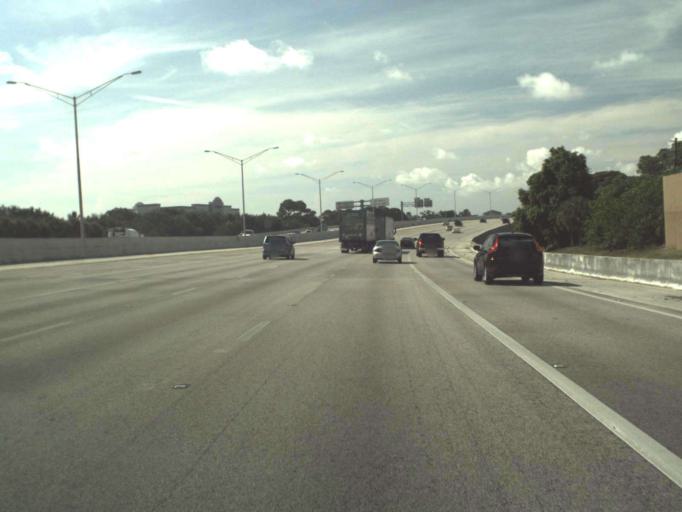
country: US
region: Florida
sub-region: Palm Beach County
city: North Palm Beach
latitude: 26.8353
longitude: -80.0994
